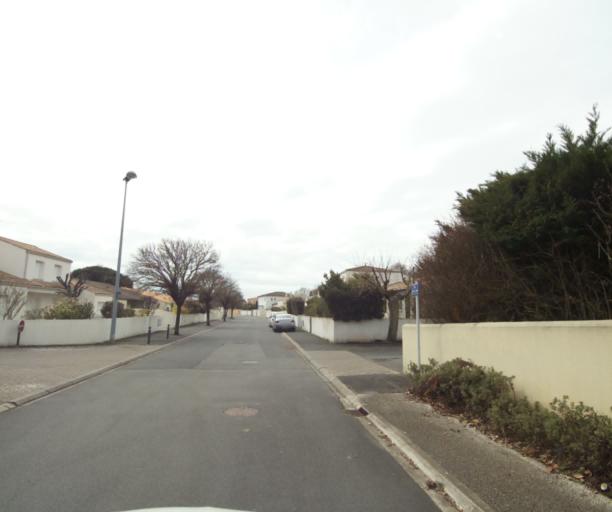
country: FR
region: Poitou-Charentes
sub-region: Departement de la Charente-Maritime
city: Lagord
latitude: 46.1837
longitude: -1.1645
